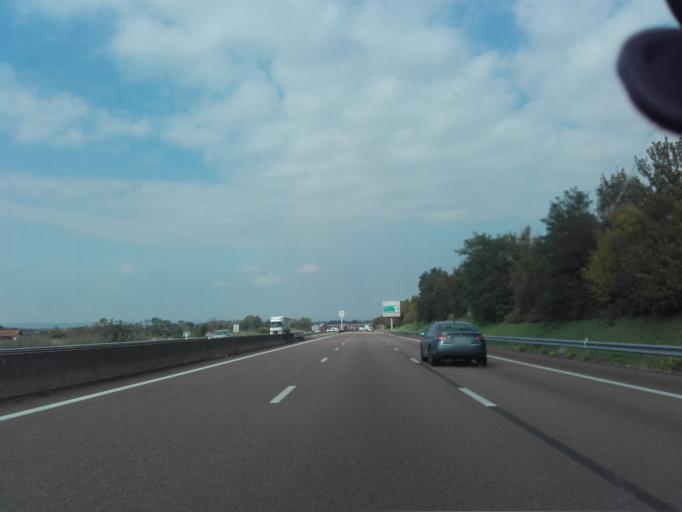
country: FR
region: Bourgogne
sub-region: Departement de Saone-et-Loire
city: Sevrey
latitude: 46.7358
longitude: 4.8354
